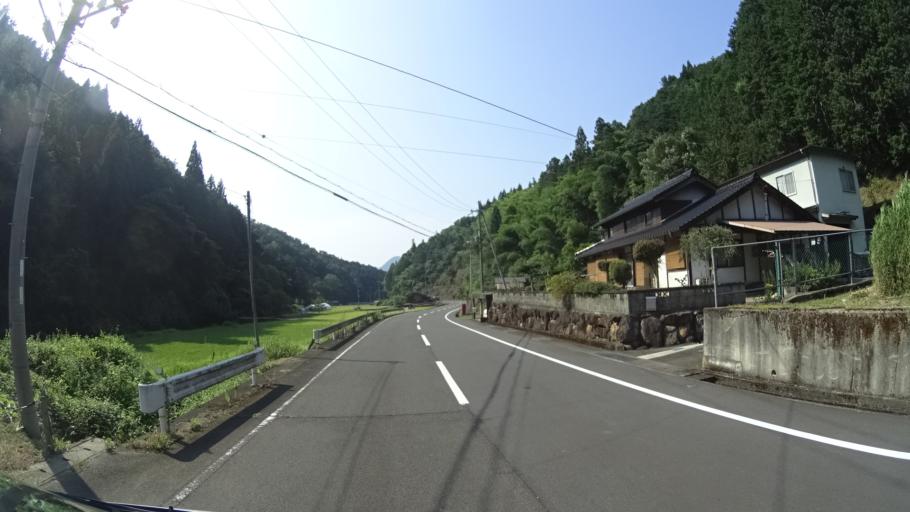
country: JP
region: Kyoto
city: Maizuru
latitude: 35.4159
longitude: 135.2292
